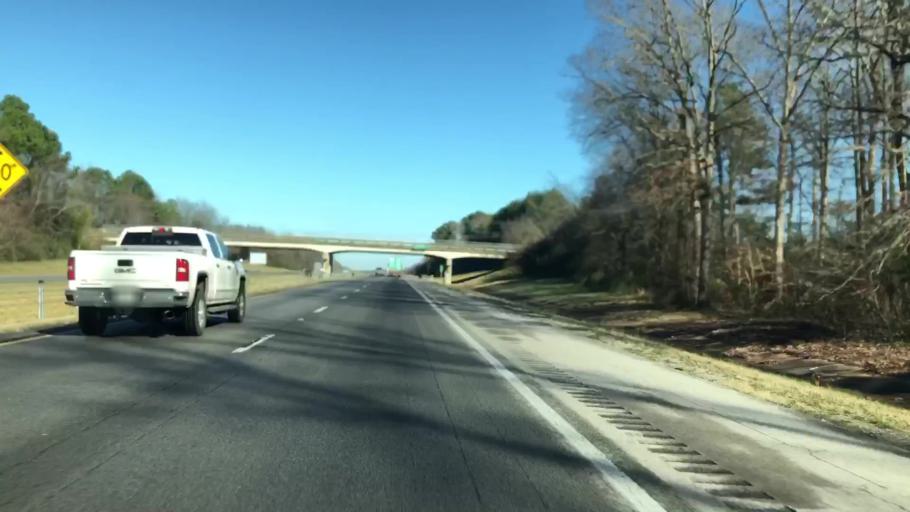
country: US
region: Alabama
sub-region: Limestone County
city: Athens
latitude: 34.7957
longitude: -86.9390
